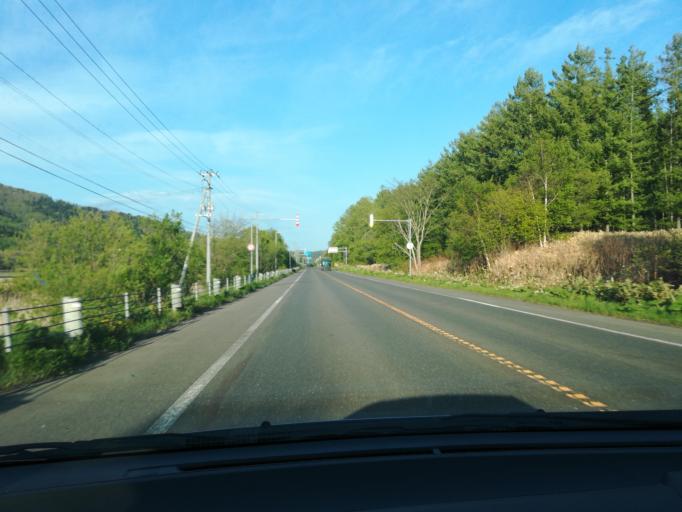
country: JP
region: Hokkaido
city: Shimo-furano
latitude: 43.1391
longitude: 142.6157
